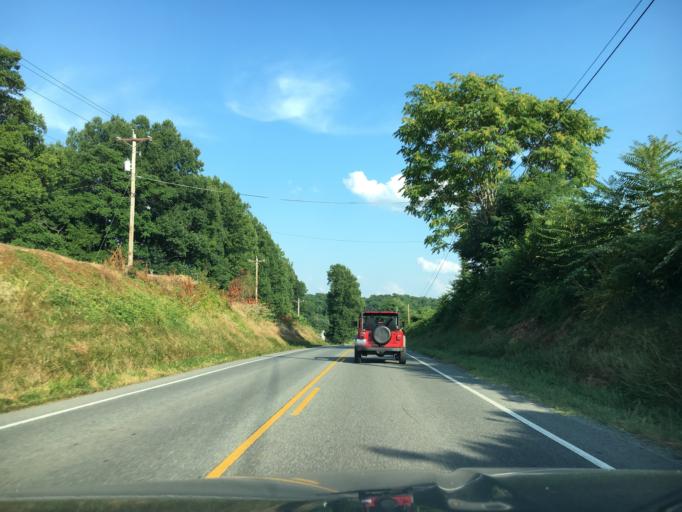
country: US
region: Virginia
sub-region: Franklin County
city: Union Hall
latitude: 37.0090
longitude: -79.7810
